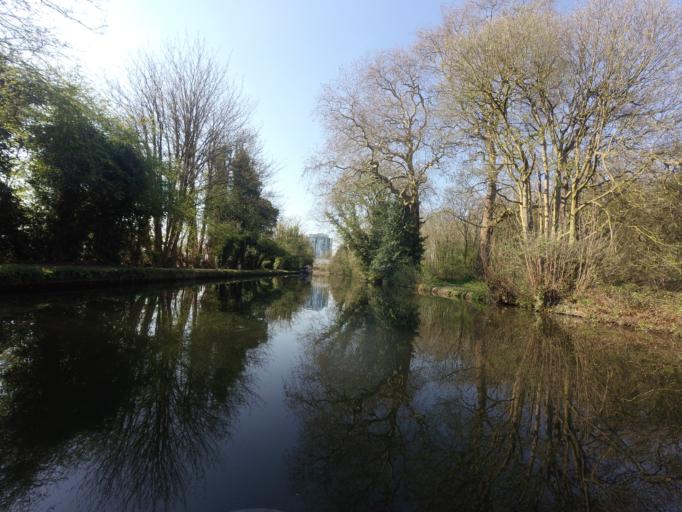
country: GB
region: England
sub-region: Hertfordshire
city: Hemel Hempstead
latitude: 51.7412
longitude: -0.4708
